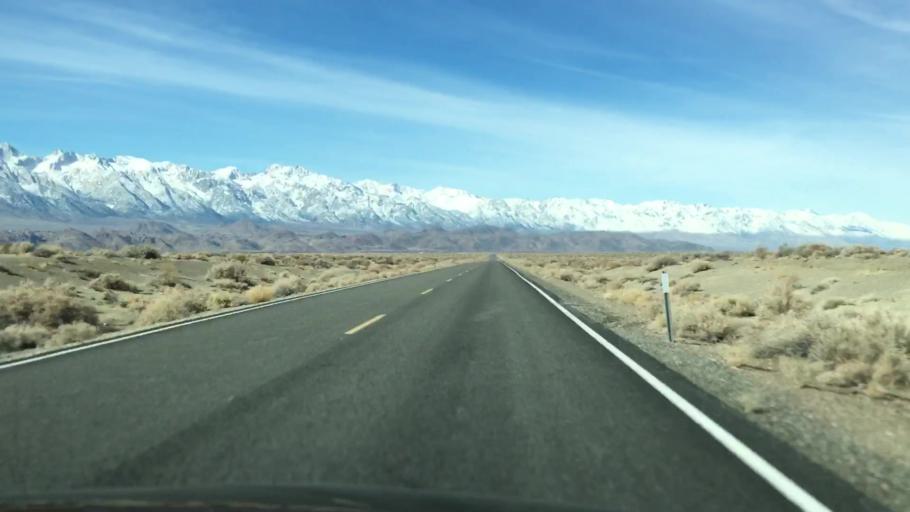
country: US
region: California
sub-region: Inyo County
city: Lone Pine
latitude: 36.5562
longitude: -117.9601
